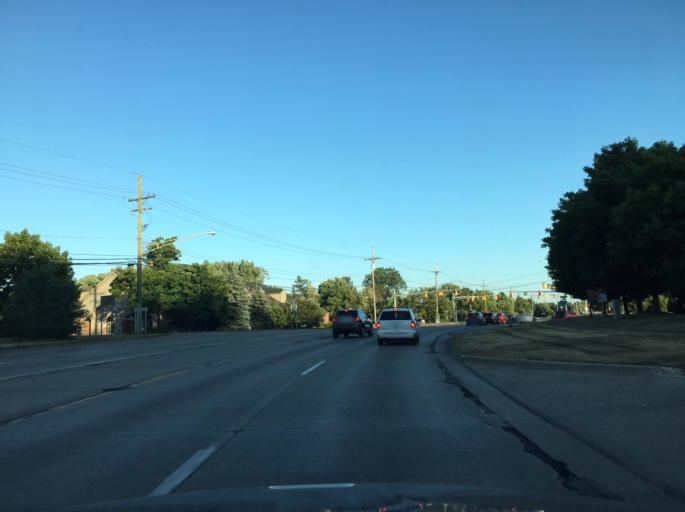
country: US
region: Michigan
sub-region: Macomb County
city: Fraser
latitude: 42.5678
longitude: -82.9677
